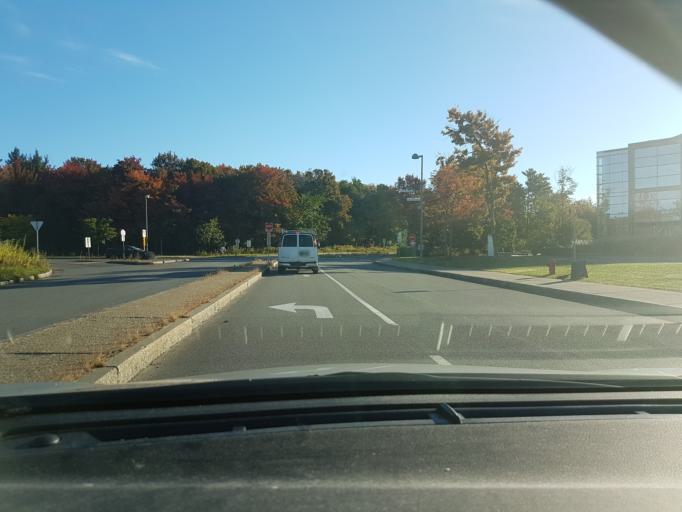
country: CA
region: Quebec
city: L'Ancienne-Lorette
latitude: 46.7963
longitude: -71.3142
